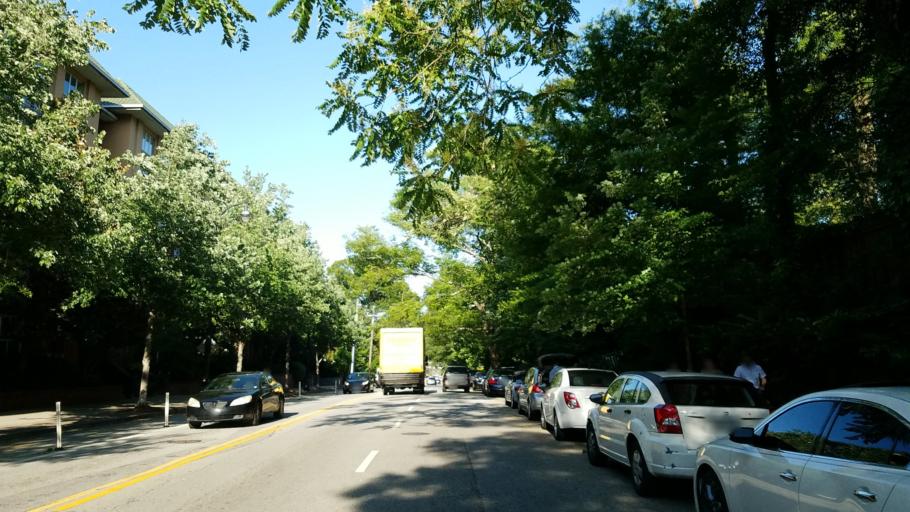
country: US
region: Georgia
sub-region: Fulton County
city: Atlanta
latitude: 33.7817
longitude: -84.3791
